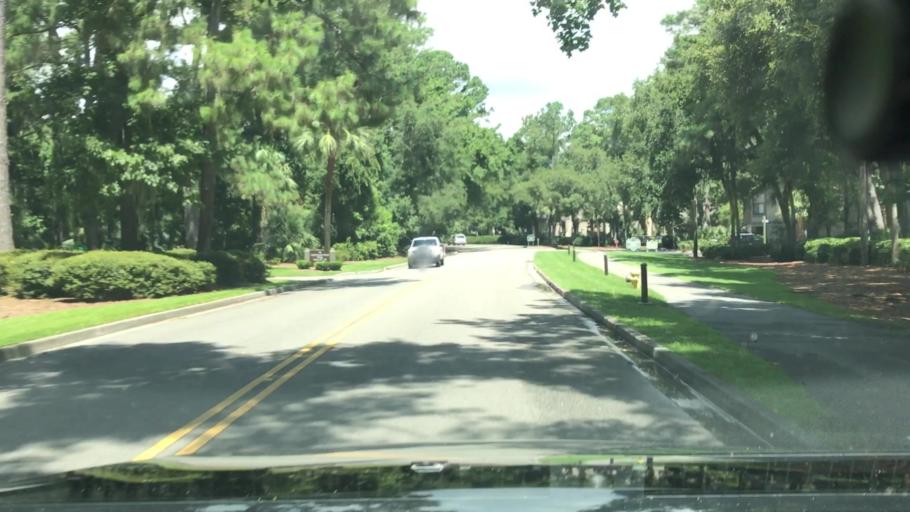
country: US
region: South Carolina
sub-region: Beaufort County
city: Hilton Head Island
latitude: 32.1292
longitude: -80.7934
